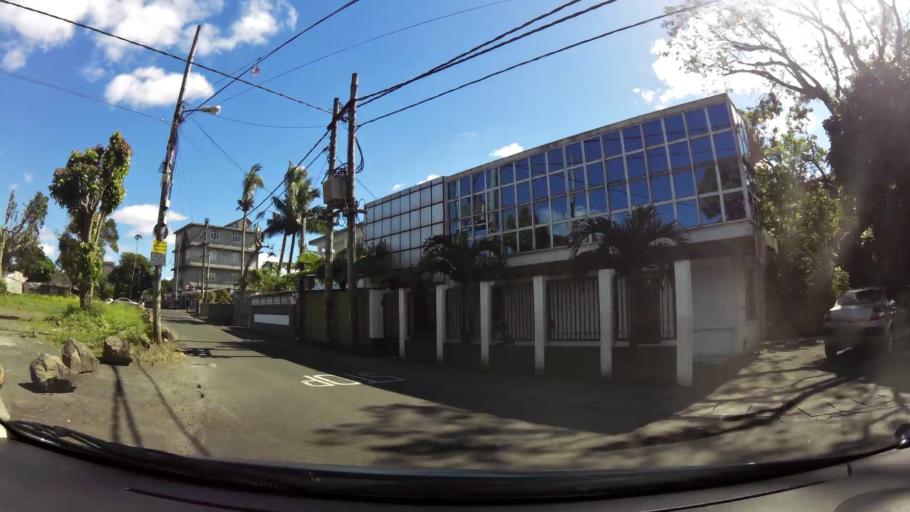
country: MU
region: Plaines Wilhems
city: Vacoas
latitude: -20.3058
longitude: 57.4851
